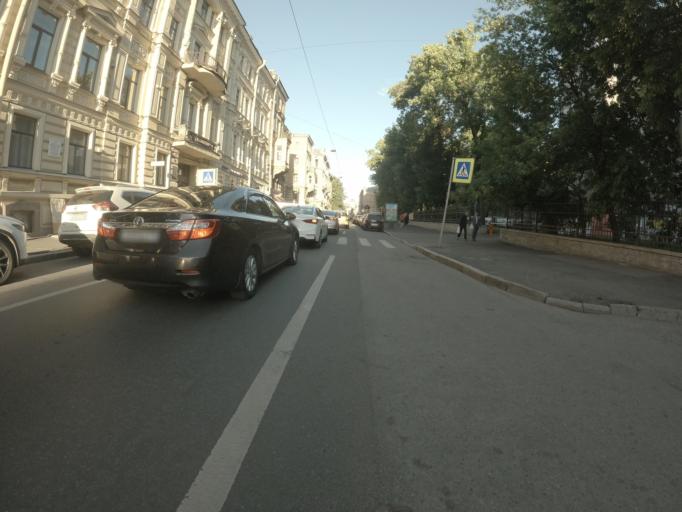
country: RU
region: St.-Petersburg
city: Centralniy
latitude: 59.9274
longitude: 30.3389
